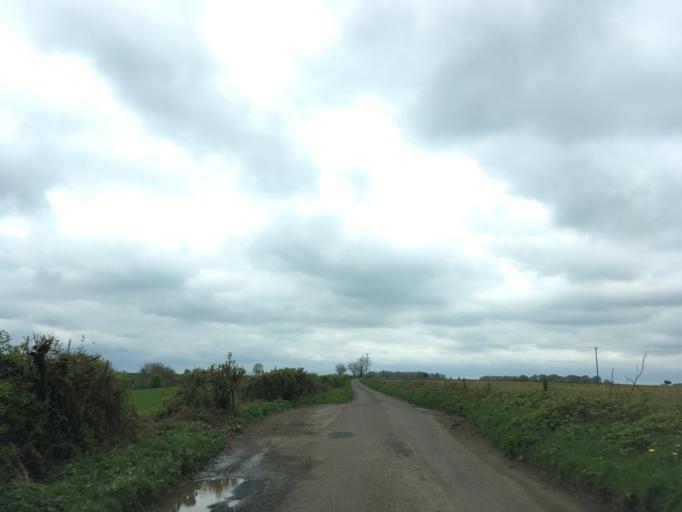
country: GB
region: England
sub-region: Gloucestershire
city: Wotton-under-Edge
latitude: 51.6554
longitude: -2.3001
